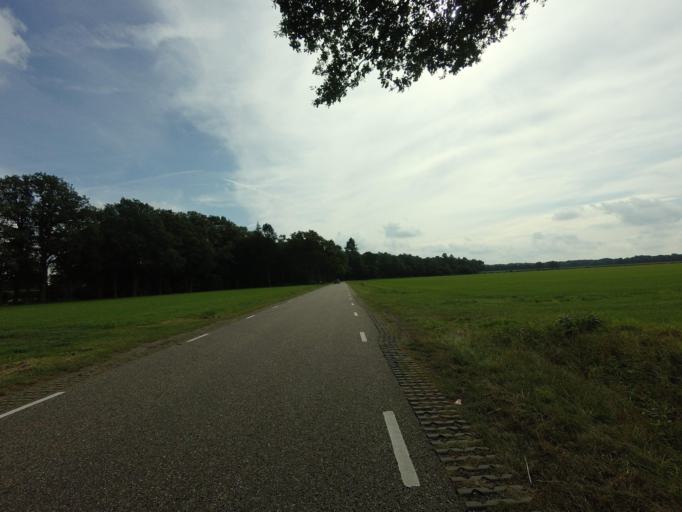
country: NL
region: Overijssel
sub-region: Gemeente Losser
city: Losser
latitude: 52.3036
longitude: 7.0171
